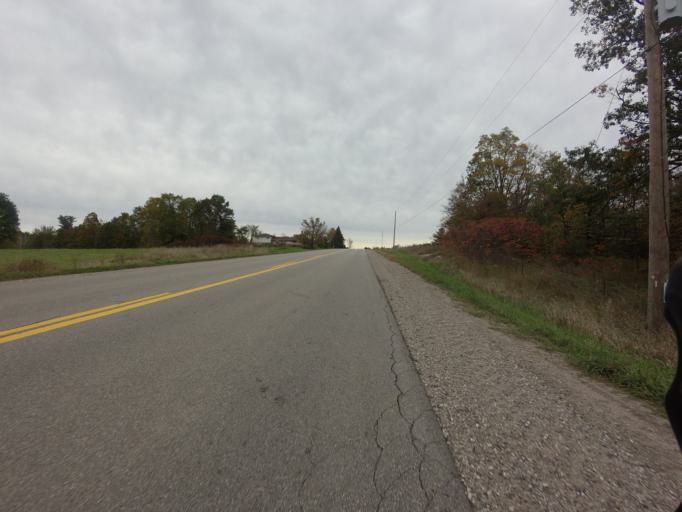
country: CA
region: Ontario
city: Gananoque
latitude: 44.5182
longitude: -76.1622
